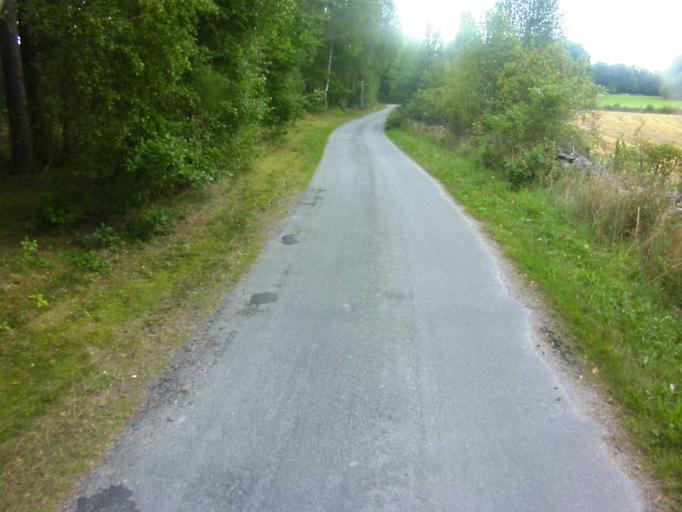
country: SE
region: Blekinge
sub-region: Solvesborgs Kommun
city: Soelvesborg
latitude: 56.0075
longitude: 14.6251
